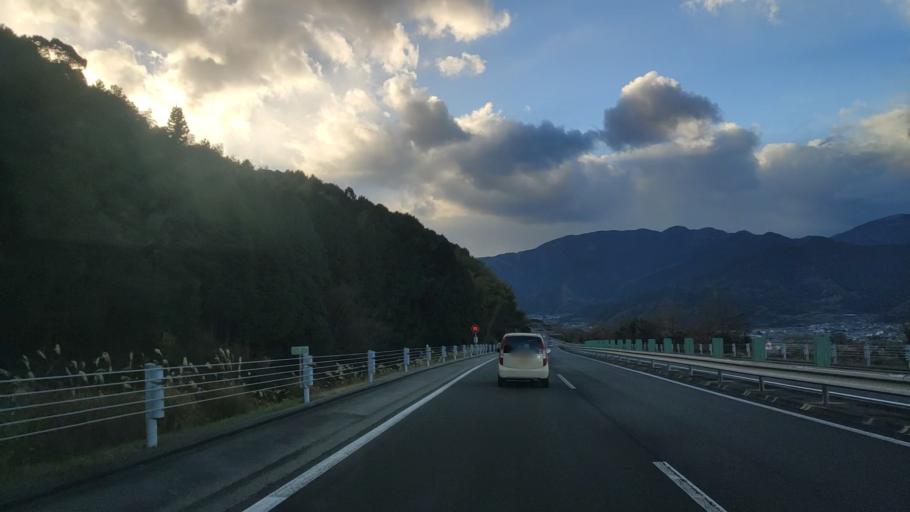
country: JP
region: Ehime
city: Saijo
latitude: 33.8560
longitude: 133.0388
